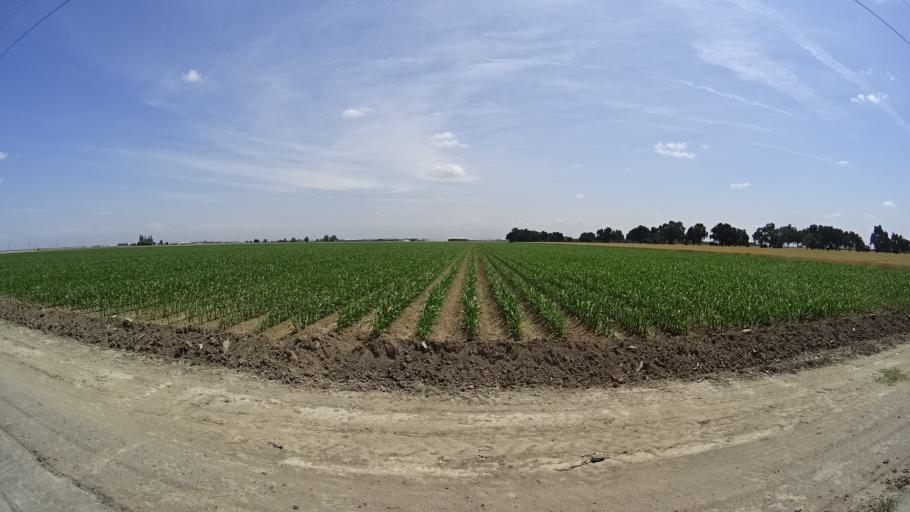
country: US
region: California
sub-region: Tulare County
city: Goshen
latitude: 36.2911
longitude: -119.4744
